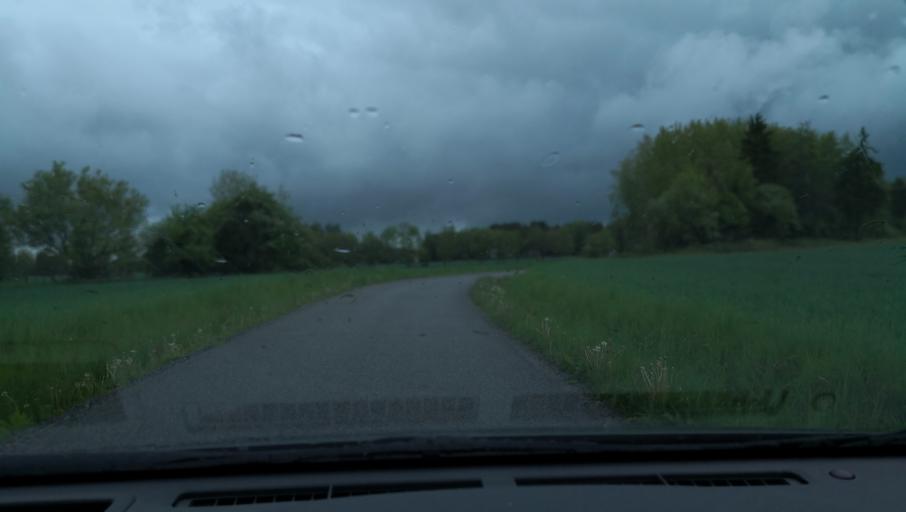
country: SE
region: Uppsala
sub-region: Enkopings Kommun
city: Orsundsbro
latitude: 59.8066
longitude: 17.3783
